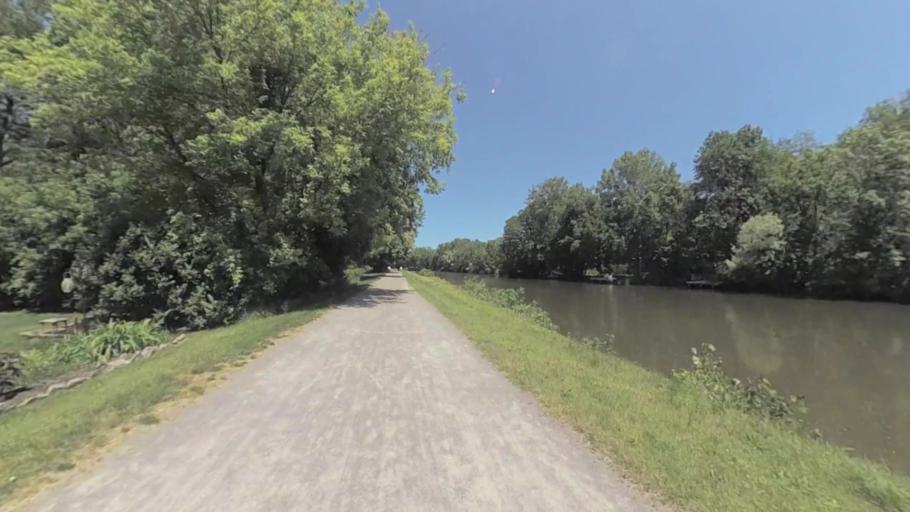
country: US
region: New York
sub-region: Monroe County
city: Fairport
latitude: 43.0955
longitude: -77.4558
